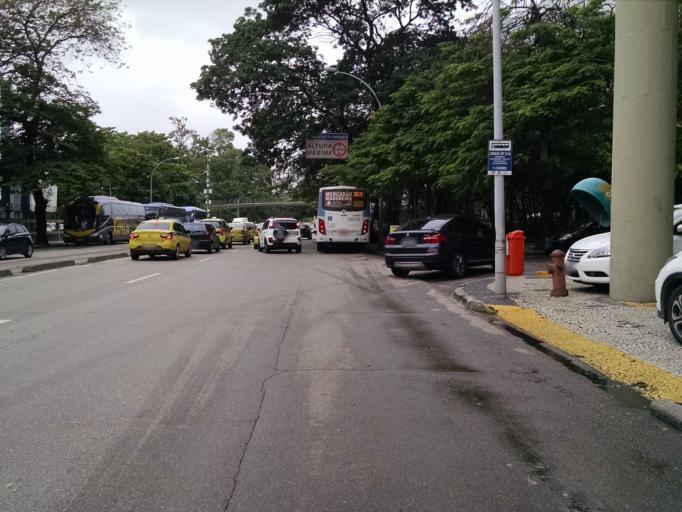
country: BR
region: Rio de Janeiro
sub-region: Rio De Janeiro
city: Rio de Janeiro
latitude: -22.9092
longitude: -43.1684
